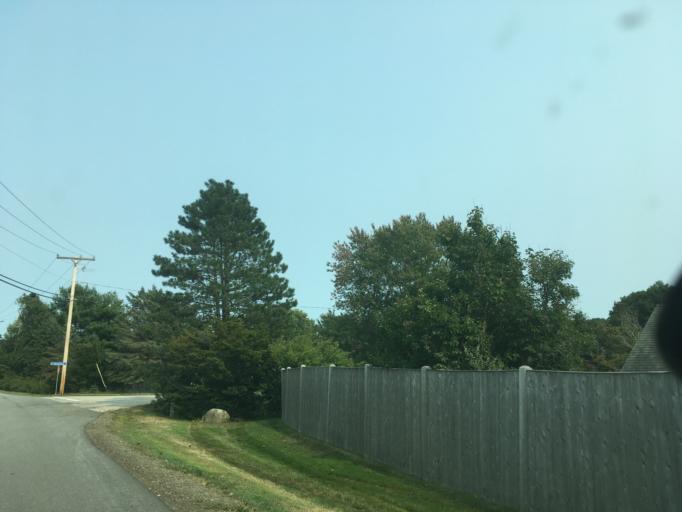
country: US
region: New Hampshire
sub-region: Rockingham County
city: North Hampton
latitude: 42.9906
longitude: -70.8864
